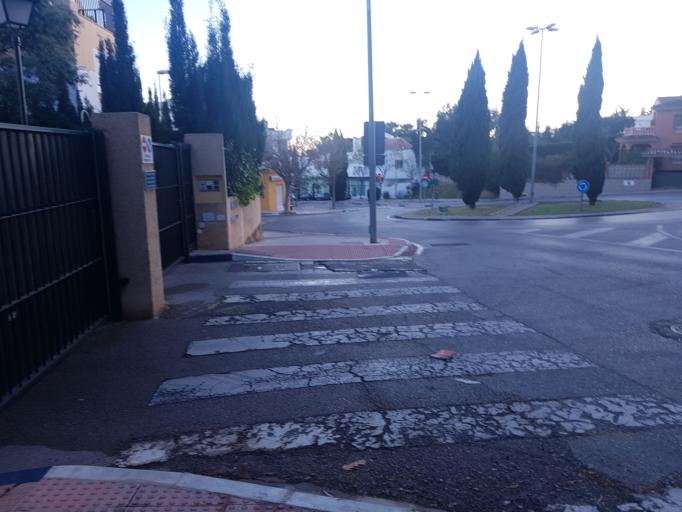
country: ES
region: Andalusia
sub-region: Provincia de Malaga
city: Marbella
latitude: 36.5238
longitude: -4.8920
